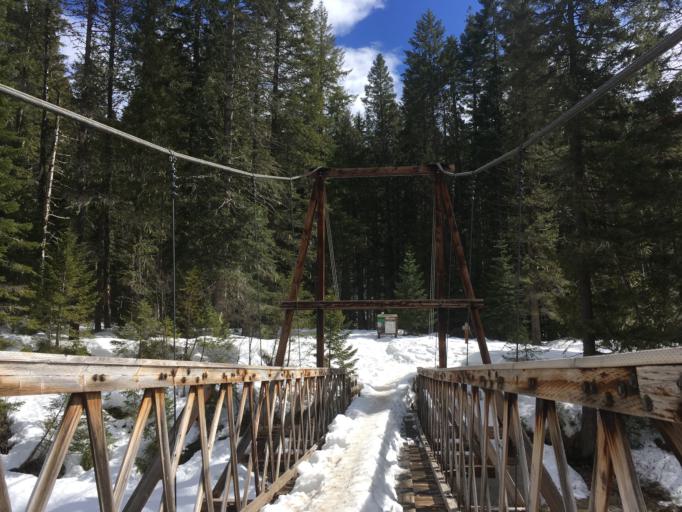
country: US
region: Montana
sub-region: Mineral County
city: Superior
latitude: 46.4743
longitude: -114.8849
